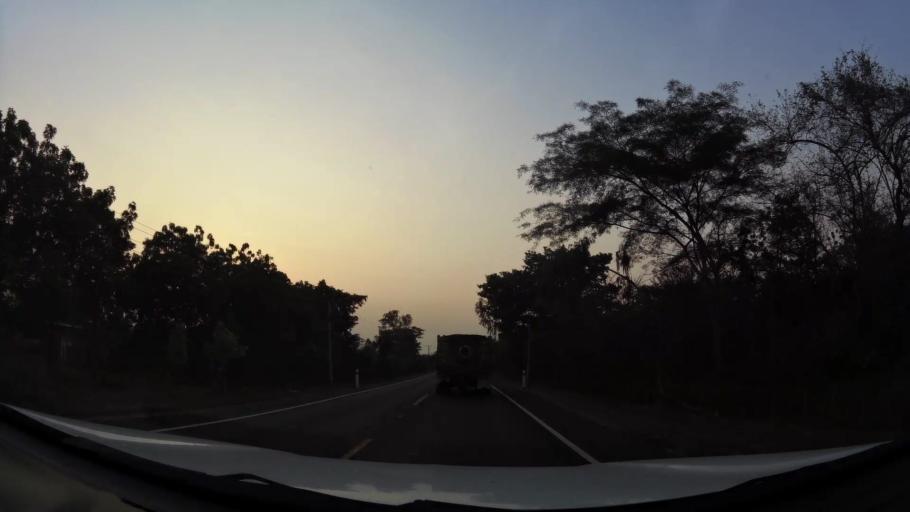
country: NI
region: Leon
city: La Paz Centro
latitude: 12.3093
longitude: -86.7821
